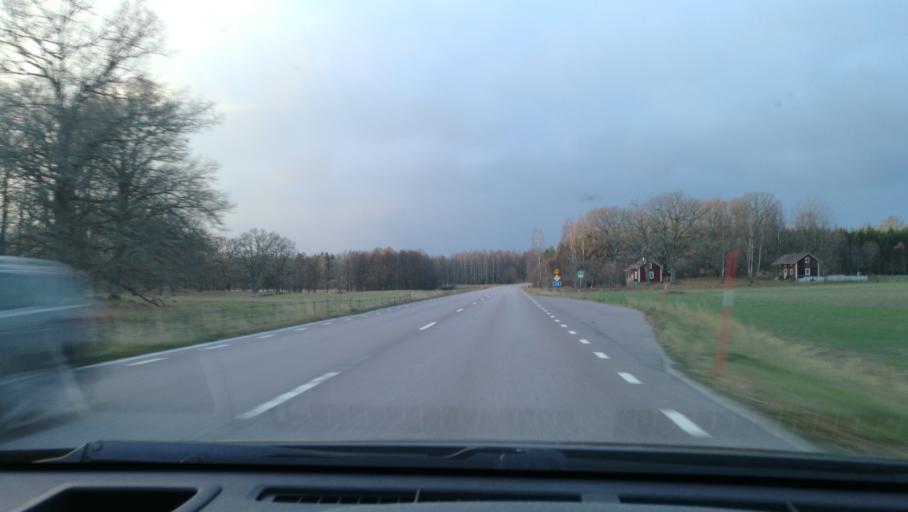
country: SE
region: Soedermanland
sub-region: Vingakers Kommun
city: Vingaker
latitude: 59.1628
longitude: 15.9964
